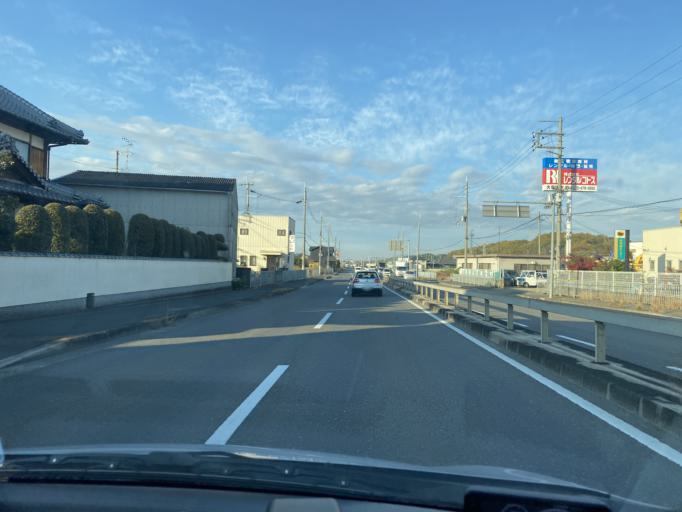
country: JP
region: Osaka
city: Izumi
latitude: 34.4334
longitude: 135.4397
